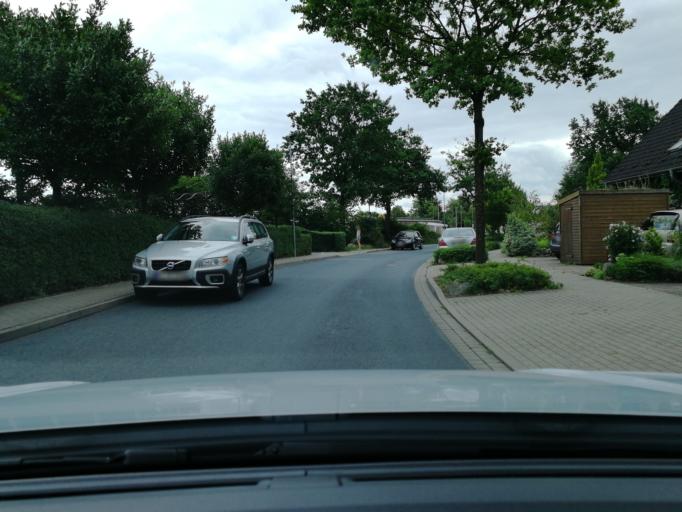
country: DE
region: Schleswig-Holstein
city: Schwarzenbek
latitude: 53.5131
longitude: 10.4879
